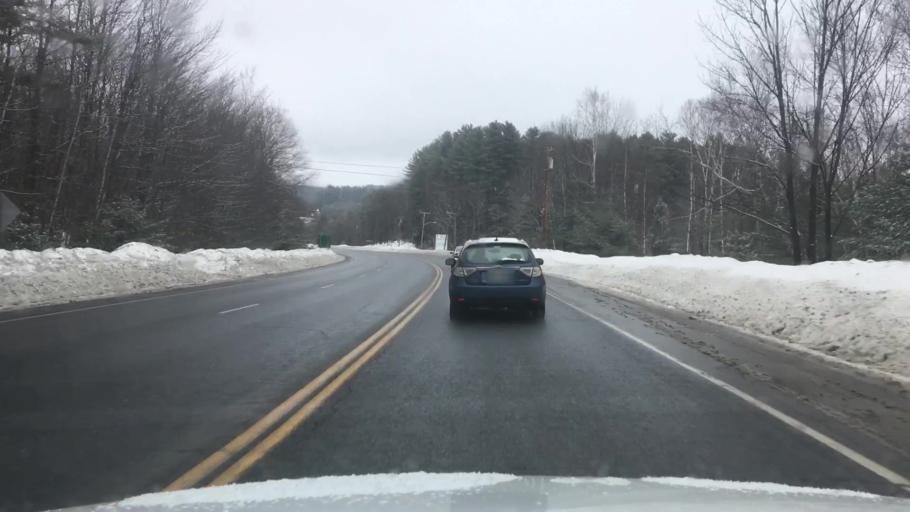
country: US
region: Maine
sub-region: Franklin County
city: Wilton
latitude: 44.5817
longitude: -70.2179
